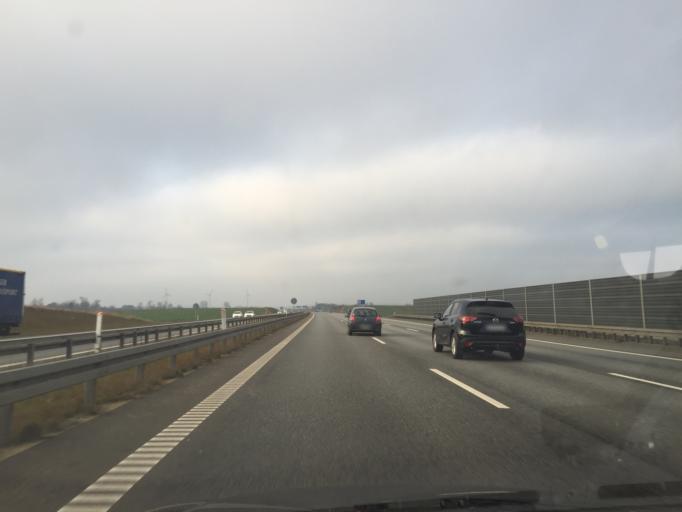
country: DK
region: South Denmark
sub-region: Middelfart Kommune
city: Norre Aby
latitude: 55.4842
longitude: 9.8595
